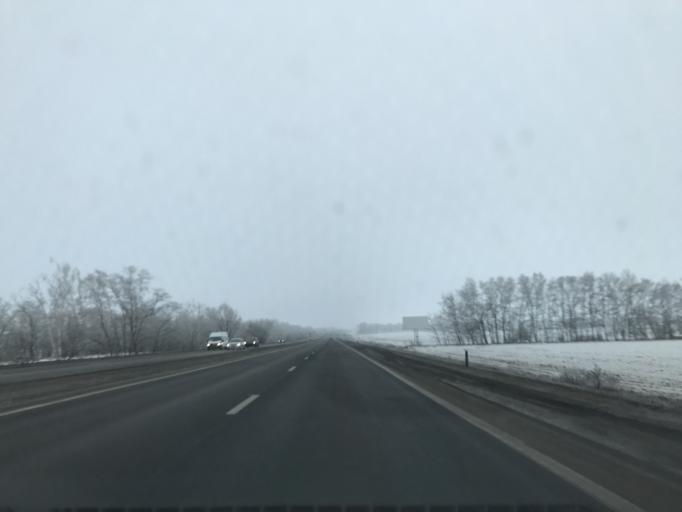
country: RU
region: Rostov
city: Grushevskaya
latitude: 47.4767
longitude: 39.9714
